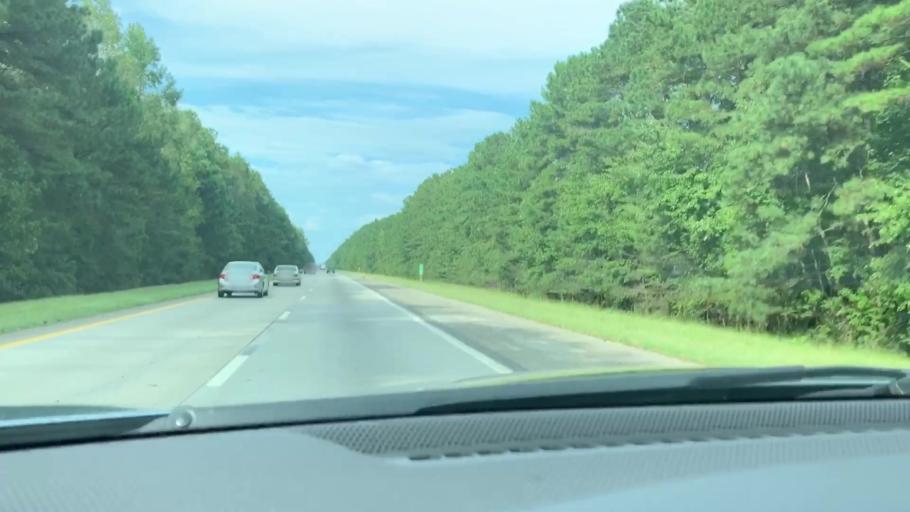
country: US
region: South Carolina
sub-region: Colleton County
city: Walterboro
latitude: 32.9663
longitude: -80.6769
